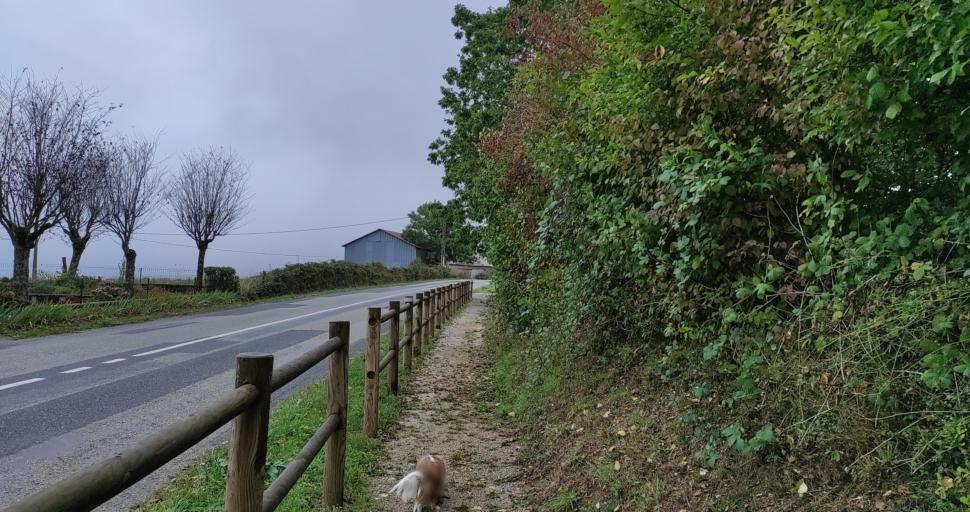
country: FR
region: Midi-Pyrenees
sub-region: Departement de l'Aveyron
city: Baraqueville
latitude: 44.2699
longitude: 2.4349
